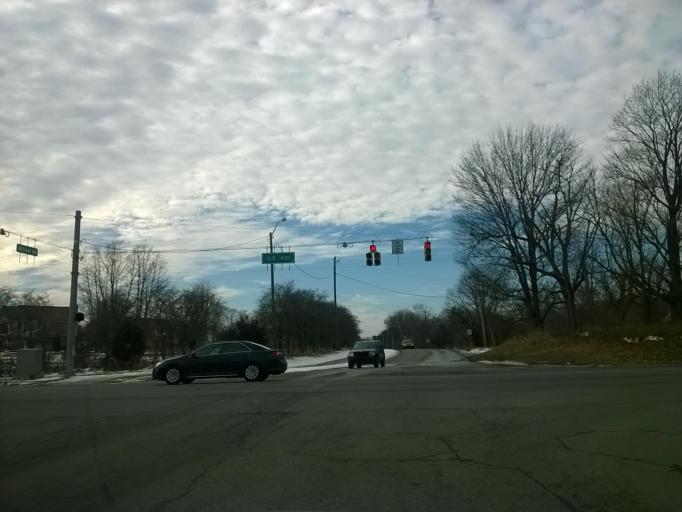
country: US
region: Indiana
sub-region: Boone County
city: Zionsville
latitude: 39.9768
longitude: -86.2540
